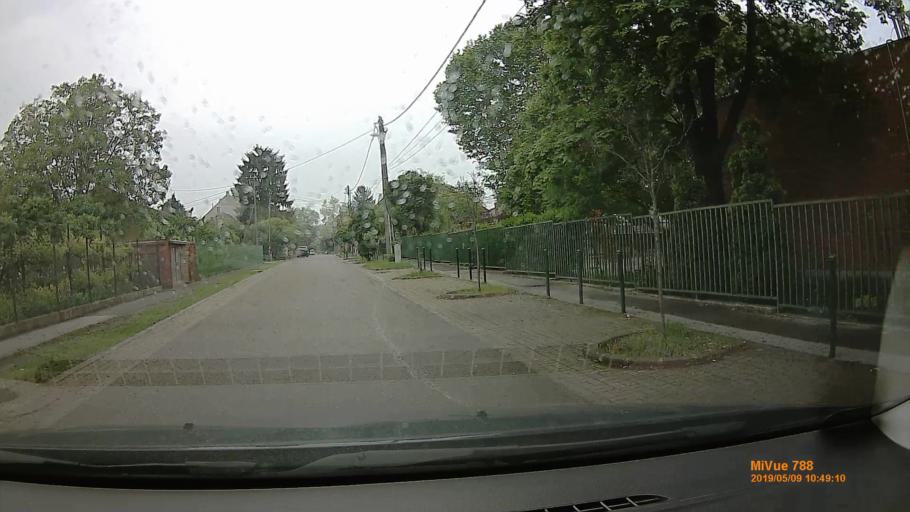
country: HU
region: Budapest
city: Budapest XVI. keruelet
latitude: 47.5197
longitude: 19.1570
